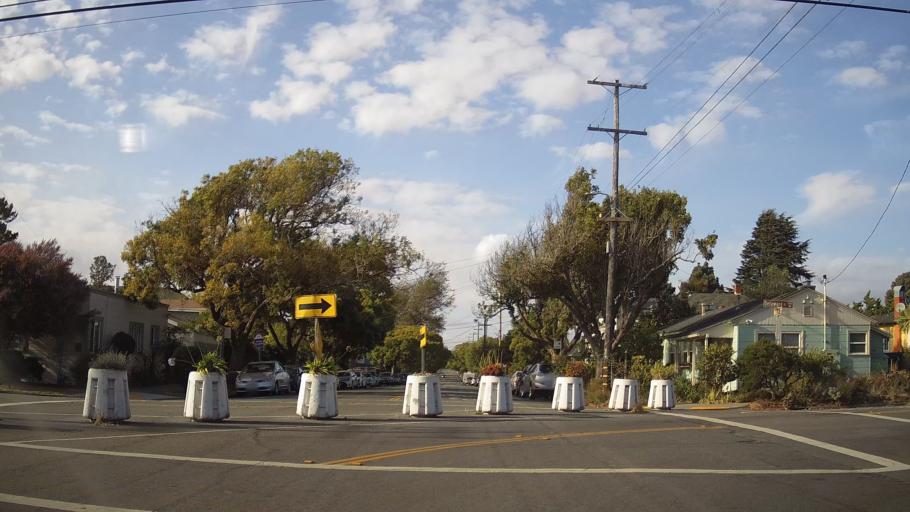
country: US
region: California
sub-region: Alameda County
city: Albany
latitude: 37.8710
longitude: -122.2952
